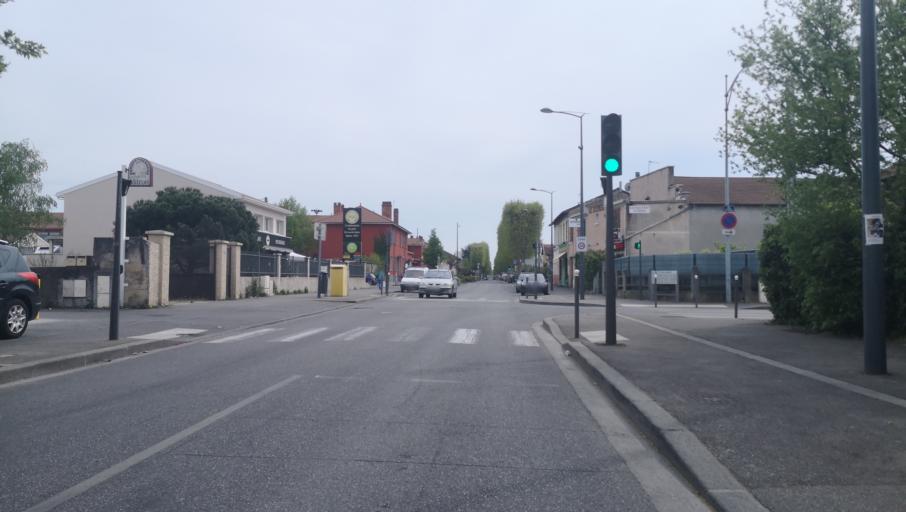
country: FR
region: Rhone-Alpes
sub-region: Departement du Rhone
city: Vaulx-en-Velin
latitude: 45.7580
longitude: 4.9287
